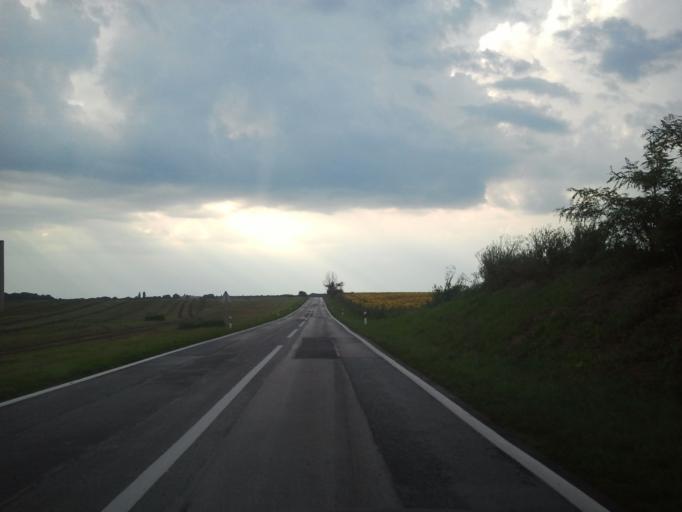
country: HR
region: Vukovarsko-Srijemska
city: Vukovar
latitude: 45.3191
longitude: 19.0685
